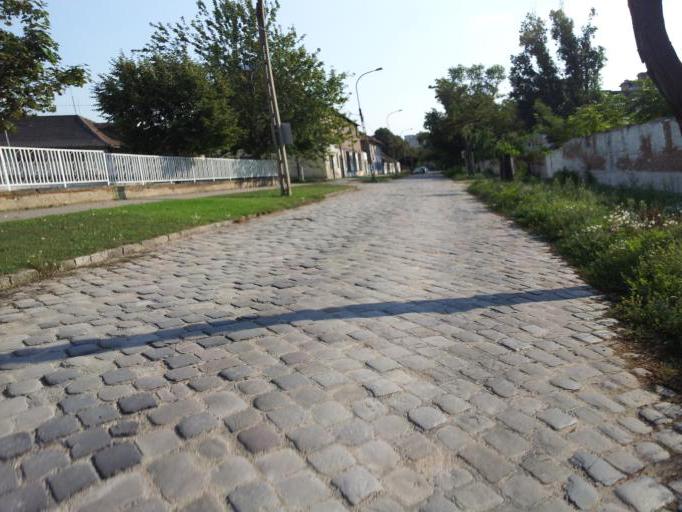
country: HU
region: Budapest
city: Budapest XIX. keruelet
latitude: 47.4727
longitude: 19.1232
